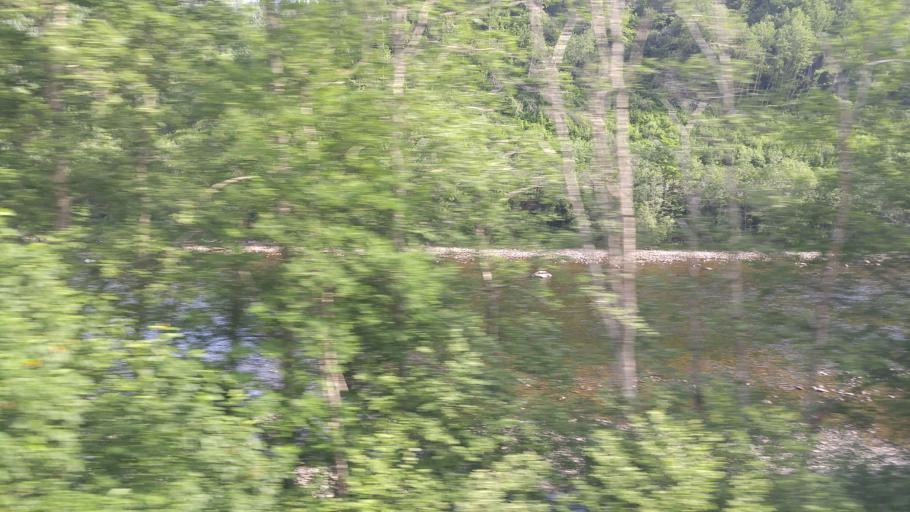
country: NO
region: Nord-Trondelag
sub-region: Levanger
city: Skogn
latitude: 63.4573
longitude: 11.2983
